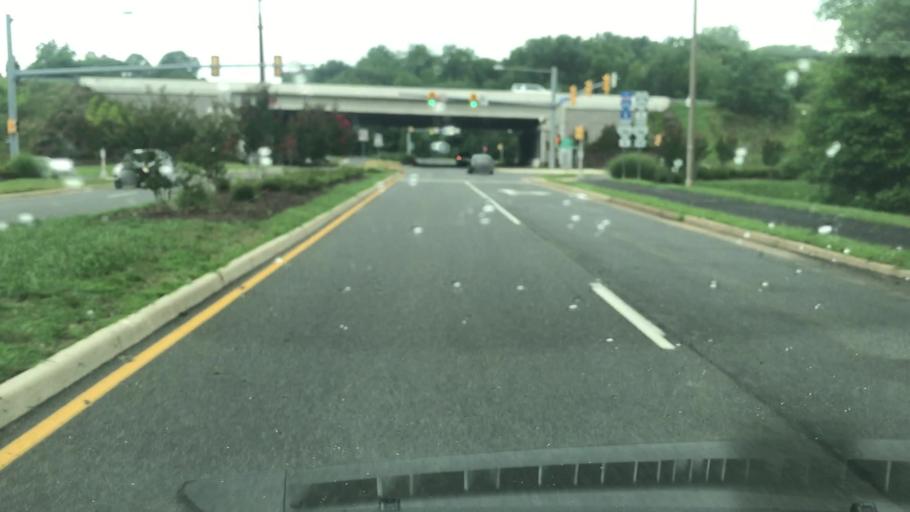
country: US
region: Virginia
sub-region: Fairfax County
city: Greenbriar
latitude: 38.8656
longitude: -77.3810
